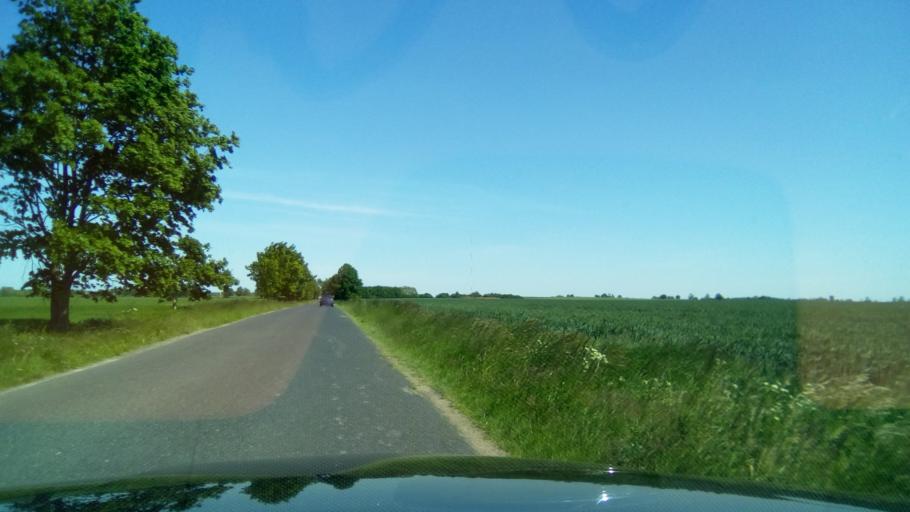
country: PL
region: Greater Poland Voivodeship
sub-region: Powiat gnieznienski
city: Niechanowo
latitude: 52.4569
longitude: 17.6240
